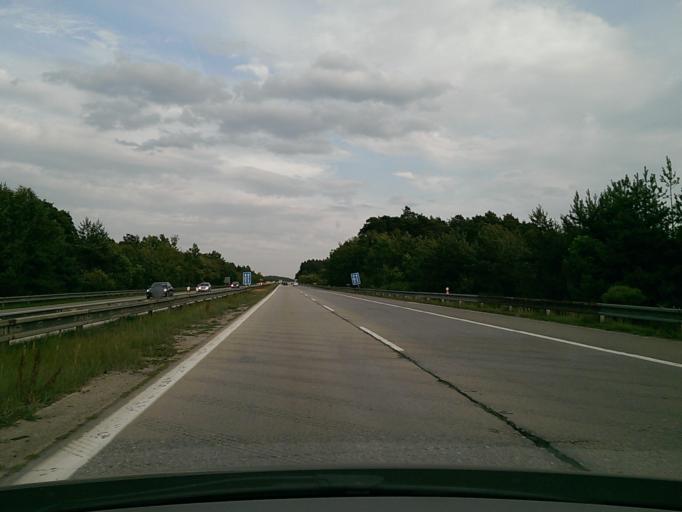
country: CZ
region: Vysocina
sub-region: Okres Zd'ar nad Sazavou
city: Velke Mezirici
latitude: 49.3353
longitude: 16.0621
